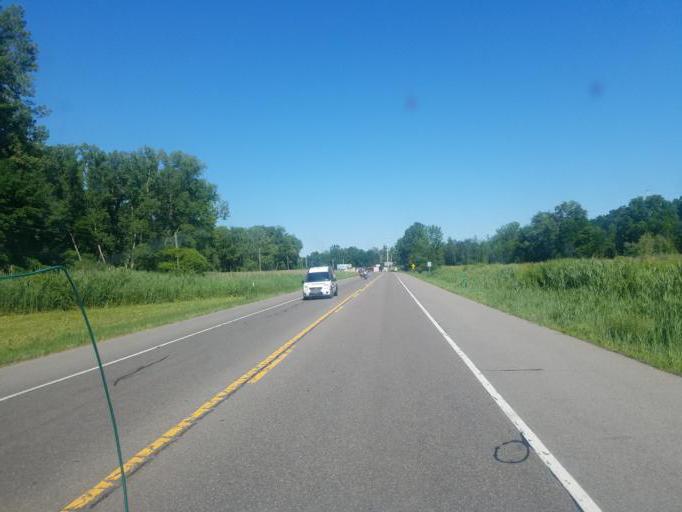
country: US
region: New York
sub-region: Wayne County
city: Lyons
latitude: 43.0591
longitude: -77.0109
